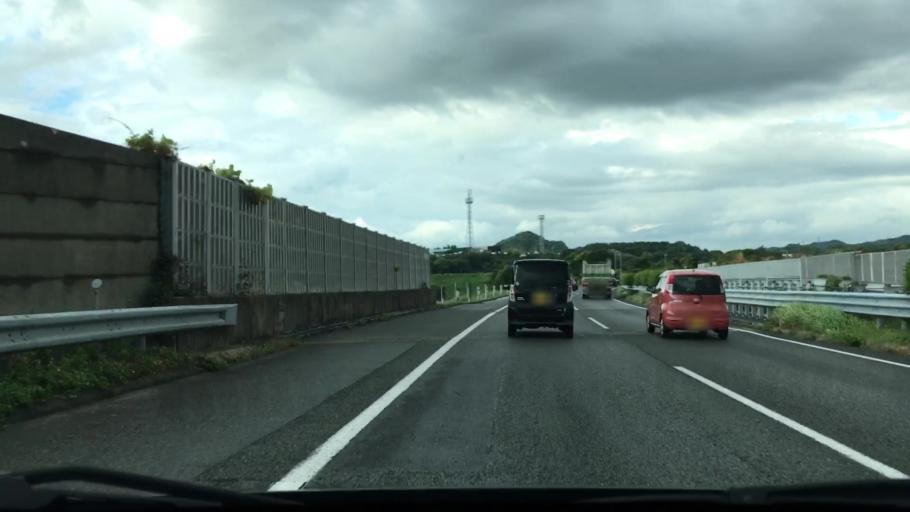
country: JP
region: Fukuoka
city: Koga
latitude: 33.7302
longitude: 130.5058
